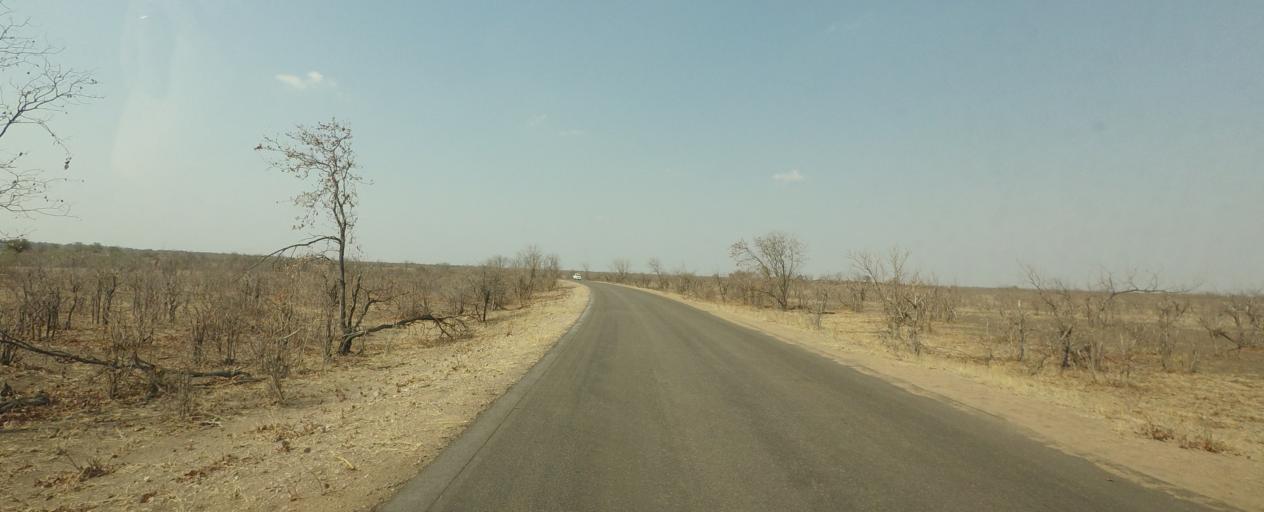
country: ZA
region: Limpopo
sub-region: Mopani District Municipality
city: Giyani
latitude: -23.1665
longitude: 31.3453
